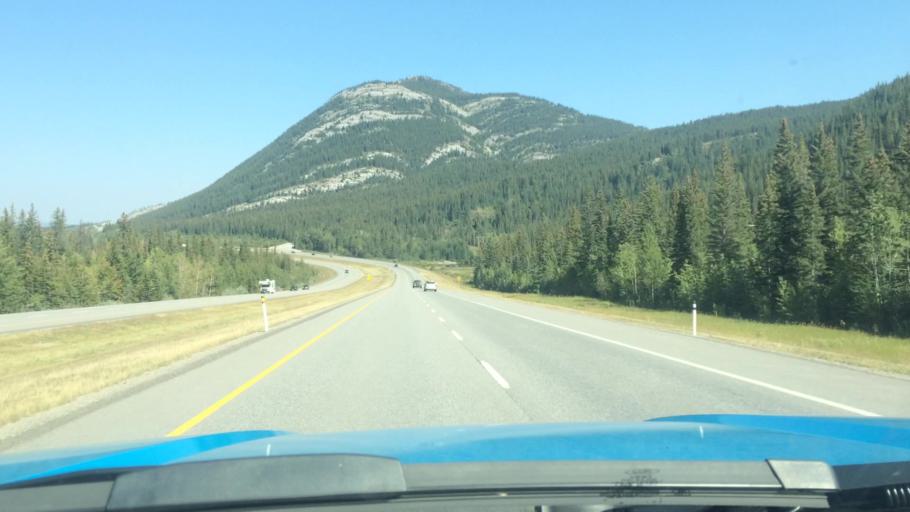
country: CA
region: Alberta
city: Canmore
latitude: 51.0525
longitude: -115.1510
